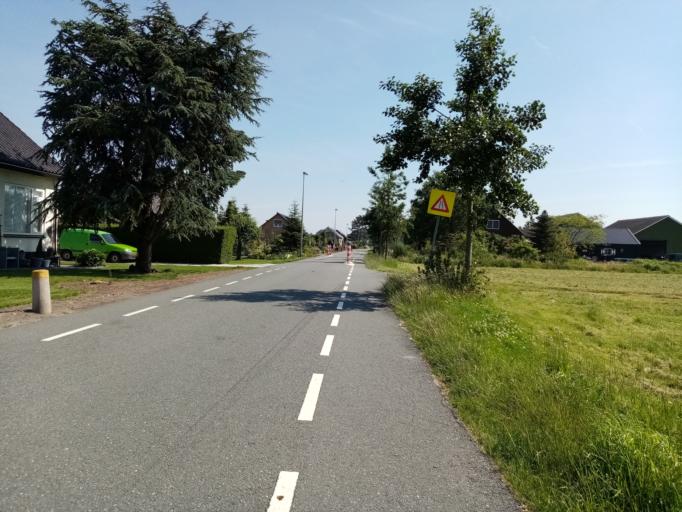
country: NL
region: South Holland
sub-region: Gemeente Nieuwkoop
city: Nieuwkoop
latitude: 52.1902
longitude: 4.7292
